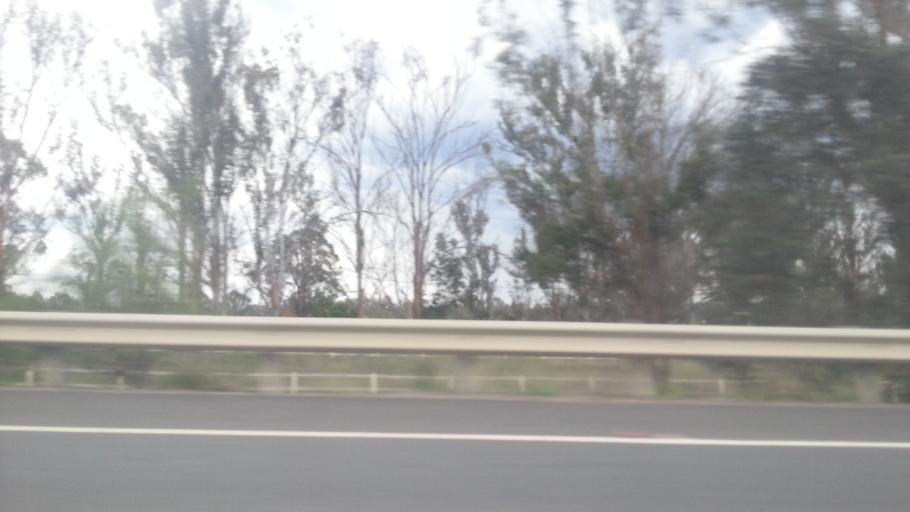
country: AU
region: New South Wales
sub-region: Penrith Municipality
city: Mulgoa
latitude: -33.8274
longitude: 150.6833
